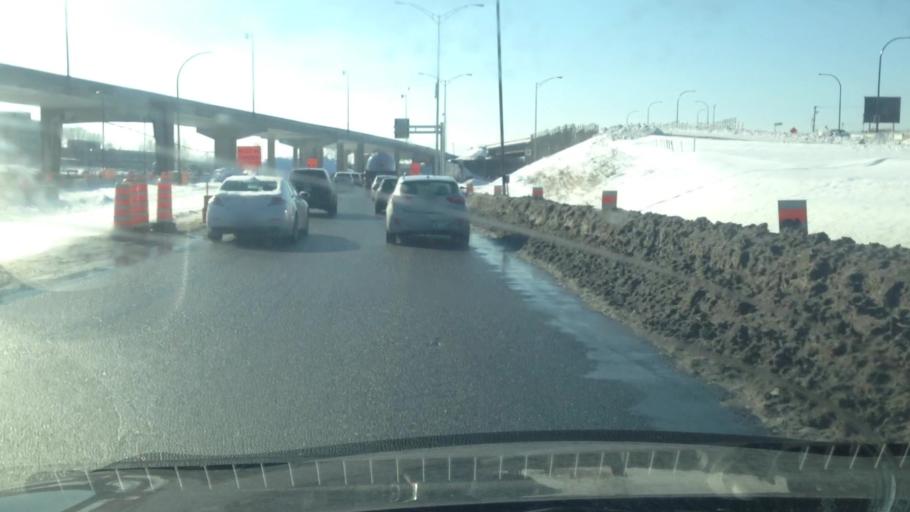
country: CA
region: Quebec
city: Montreal-Ouest
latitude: 45.4523
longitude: -73.6302
